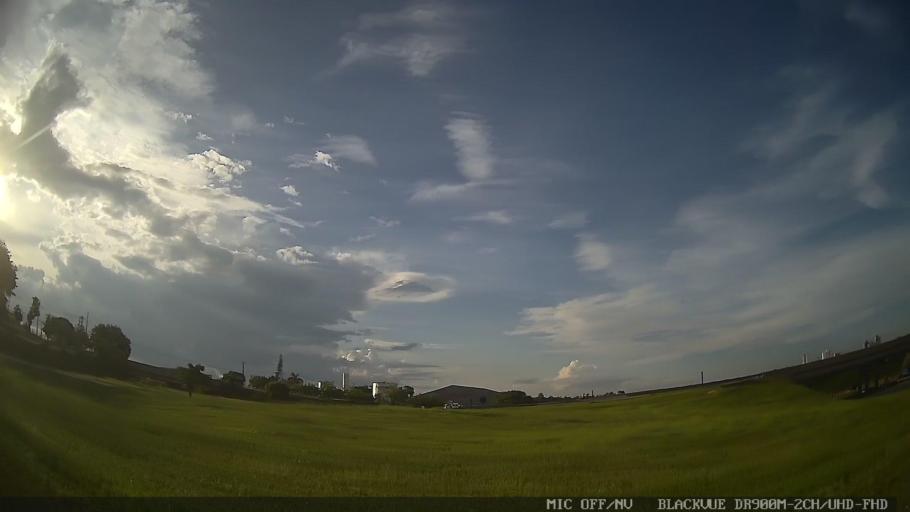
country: BR
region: Sao Paulo
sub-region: Tiete
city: Tiete
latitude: -23.1195
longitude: -47.7183
